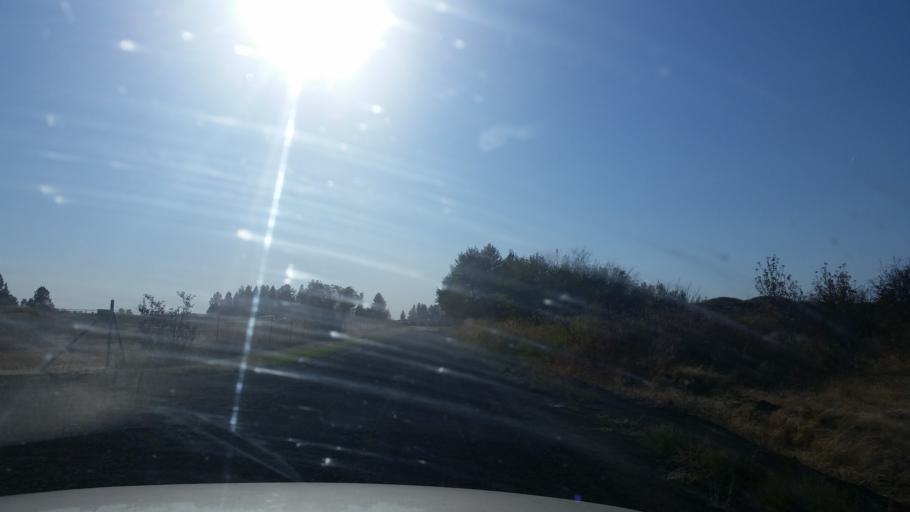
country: US
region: Washington
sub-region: Spokane County
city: Cheney
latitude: 47.3498
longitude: -117.7123
